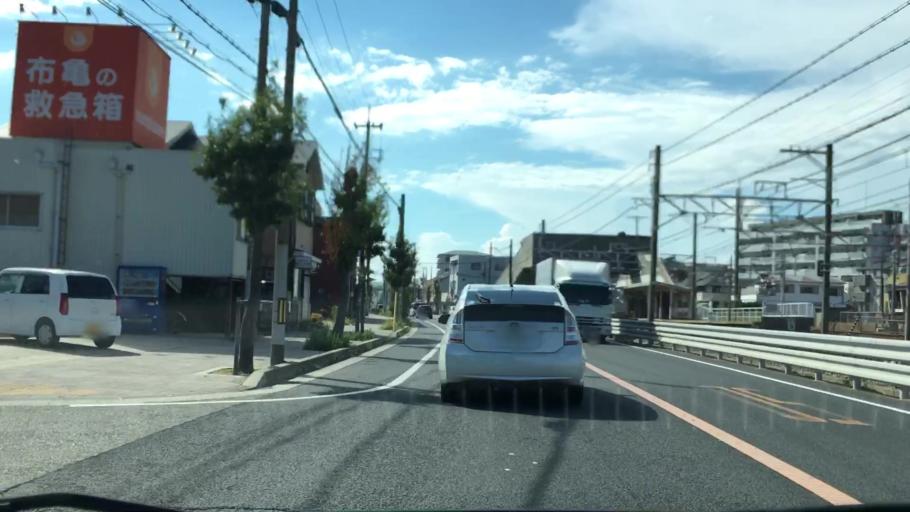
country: JP
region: Hyogo
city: Akashi
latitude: 34.6461
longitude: 135.0094
